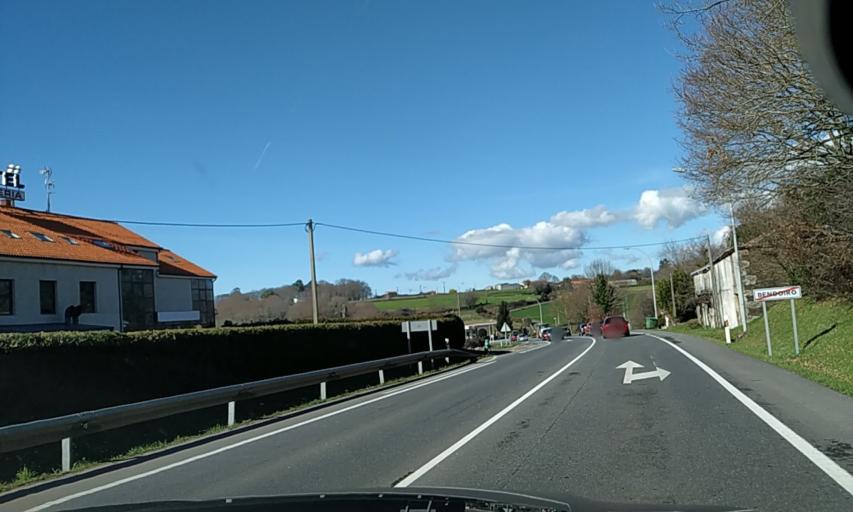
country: ES
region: Galicia
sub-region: Provincia de Pontevedra
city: Lalin
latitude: 42.6807
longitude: -8.1667
